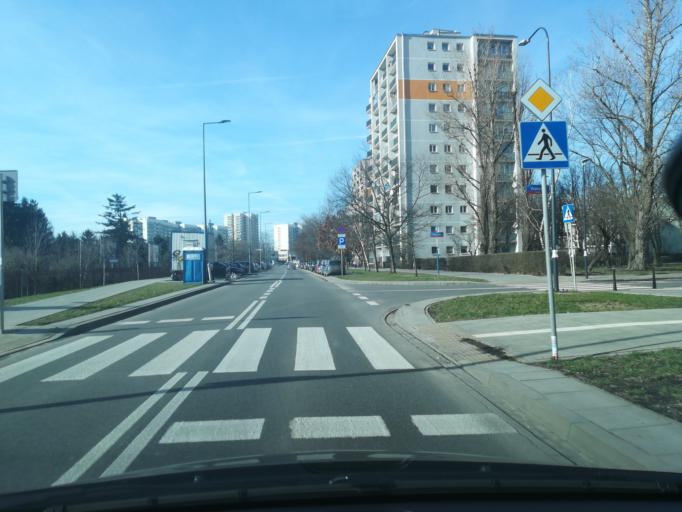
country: PL
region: Masovian Voivodeship
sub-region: Warszawa
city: Praga Poludnie
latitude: 52.2395
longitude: 21.0742
